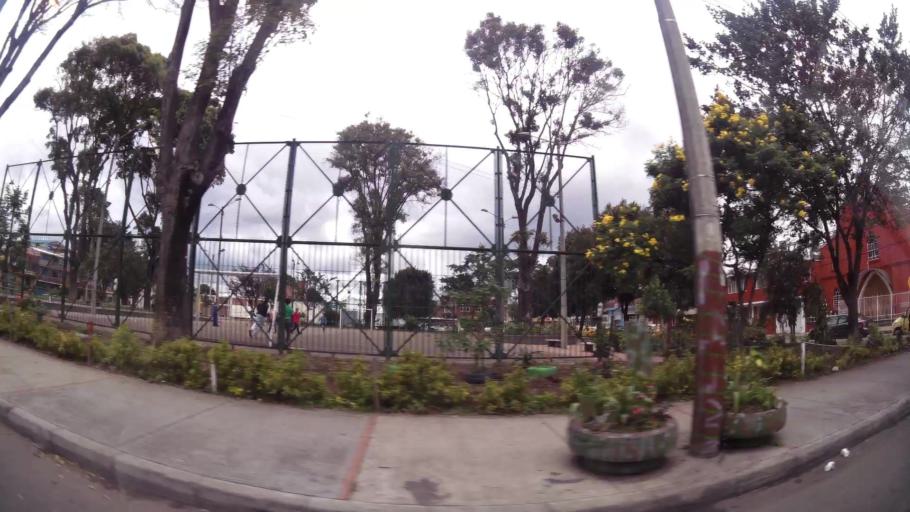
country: CO
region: Bogota D.C.
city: Barrio San Luis
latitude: 4.6980
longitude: -74.0973
